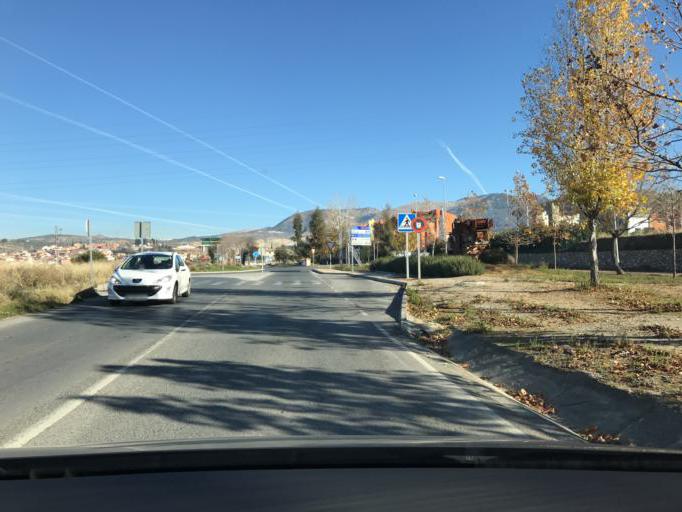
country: ES
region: Andalusia
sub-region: Provincia de Granada
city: Jun
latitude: 37.2118
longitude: -3.5935
